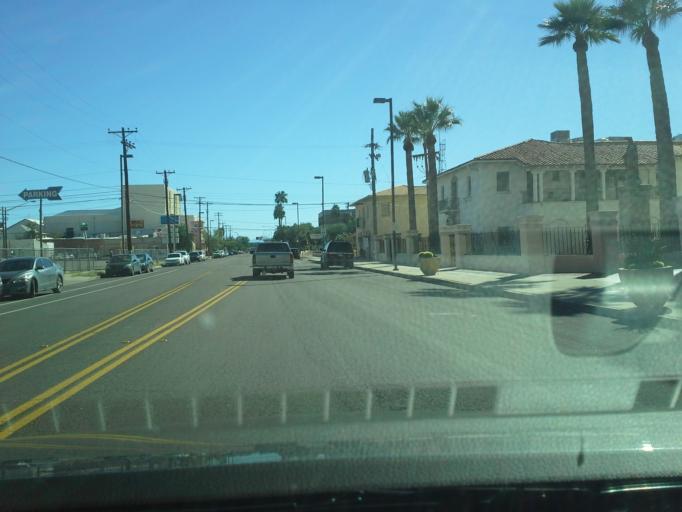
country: US
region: Arizona
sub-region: Pima County
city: South Tucson
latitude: 32.2196
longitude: -110.9709
